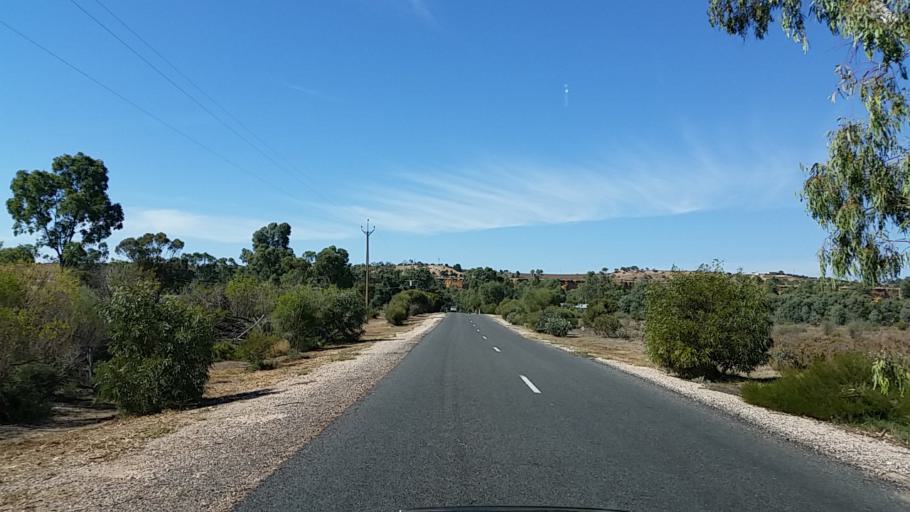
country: AU
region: South Australia
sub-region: Mid Murray
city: Mannum
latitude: -34.7066
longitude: 139.5701
